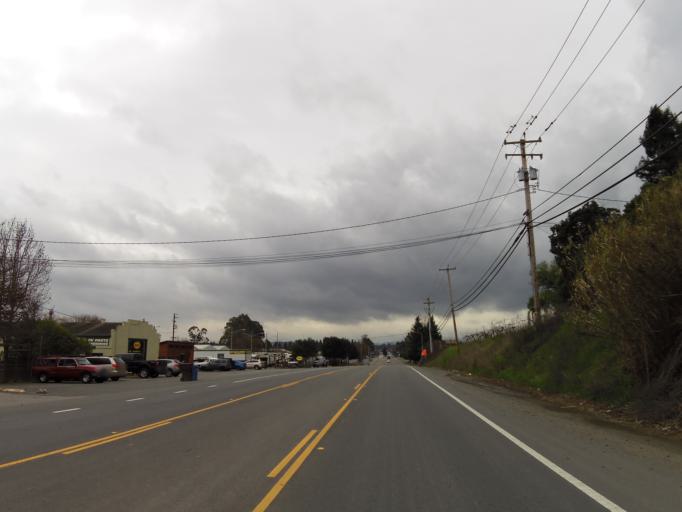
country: US
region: California
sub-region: Sonoma County
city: Penngrove
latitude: 38.2834
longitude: -122.6677
